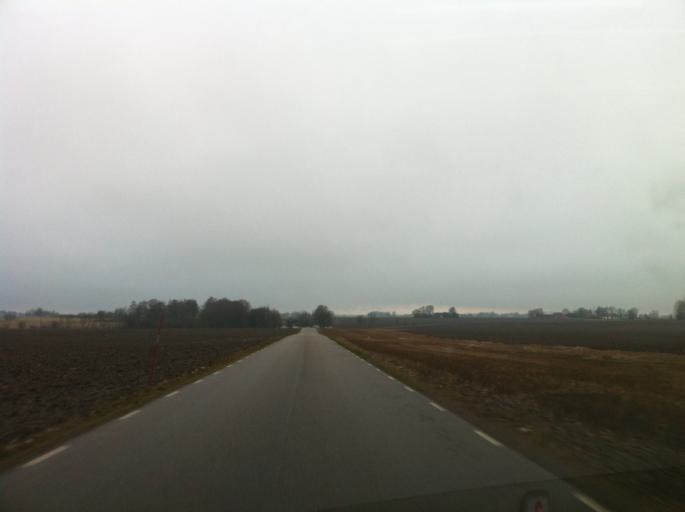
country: SE
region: Skane
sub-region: Landskrona
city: Asmundtorp
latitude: 55.9758
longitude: 12.9343
